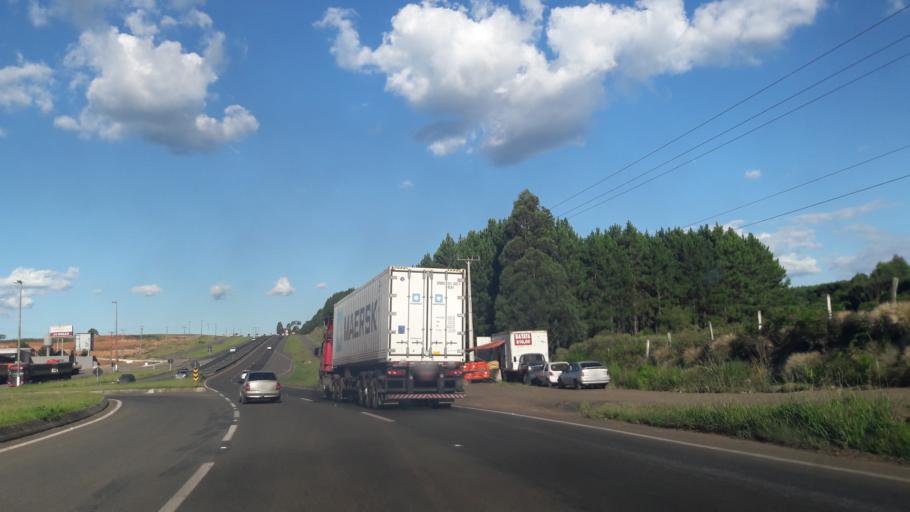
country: BR
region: Parana
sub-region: Guarapuava
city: Guarapuava
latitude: -25.3450
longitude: -51.4424
